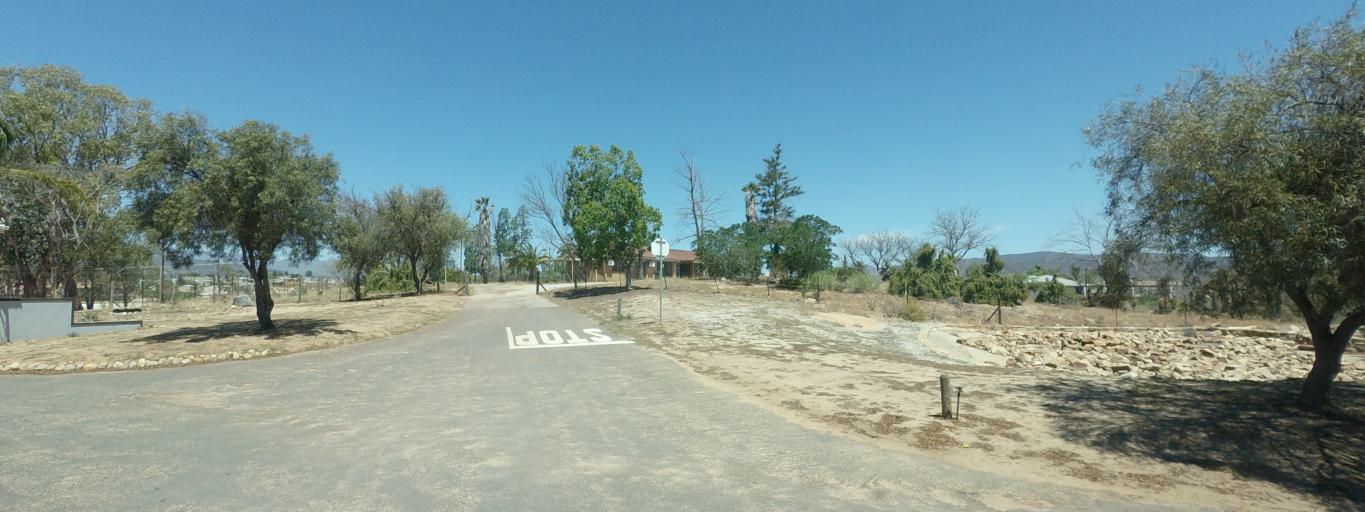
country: ZA
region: Western Cape
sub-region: West Coast District Municipality
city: Clanwilliam
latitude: -32.1901
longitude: 18.8860
